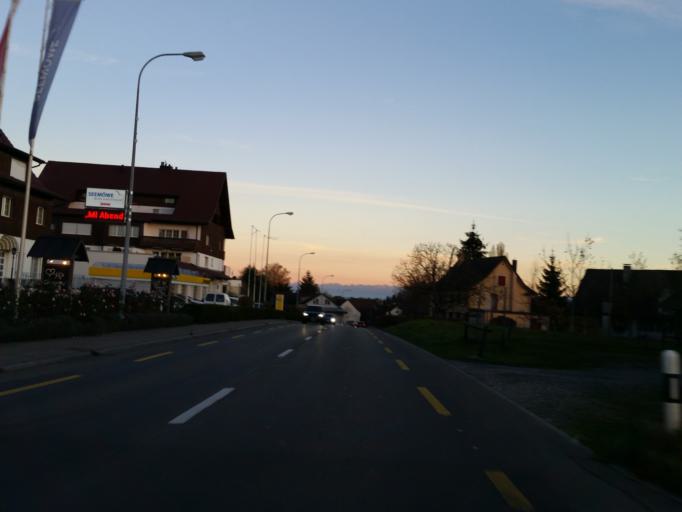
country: CH
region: Thurgau
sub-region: Kreuzlingen District
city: Guttingen
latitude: 47.6063
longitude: 9.2833
